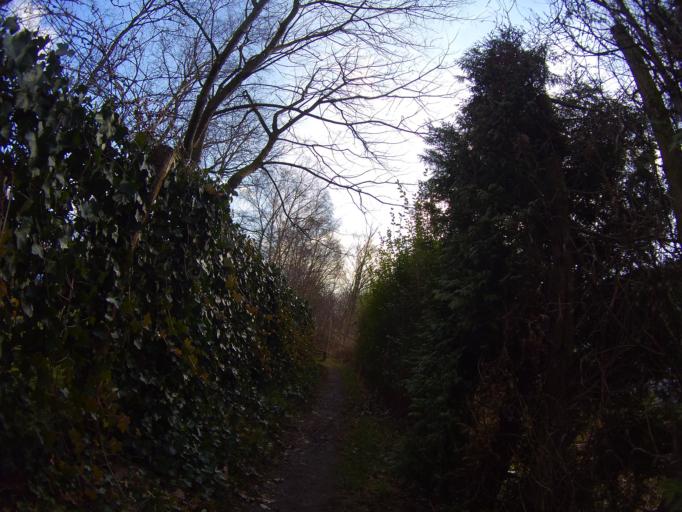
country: NL
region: Utrecht
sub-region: Gemeente Woudenberg
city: Woudenberg
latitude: 52.0797
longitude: 5.4508
